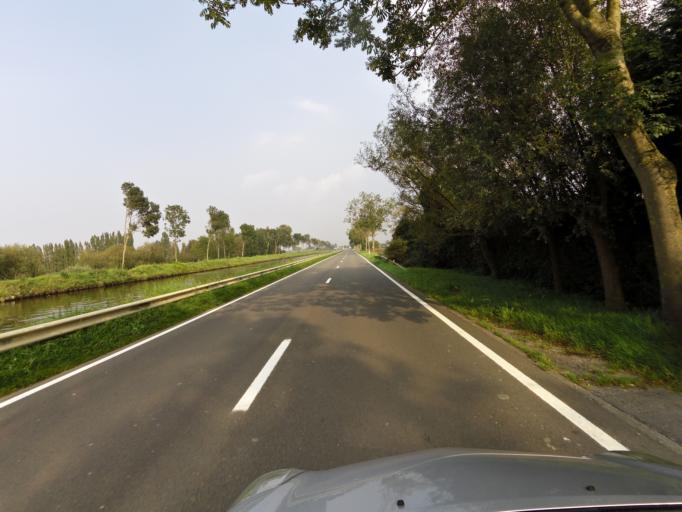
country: BE
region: Flanders
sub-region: Provincie West-Vlaanderen
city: Ostend
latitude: 51.1730
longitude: 2.8997
